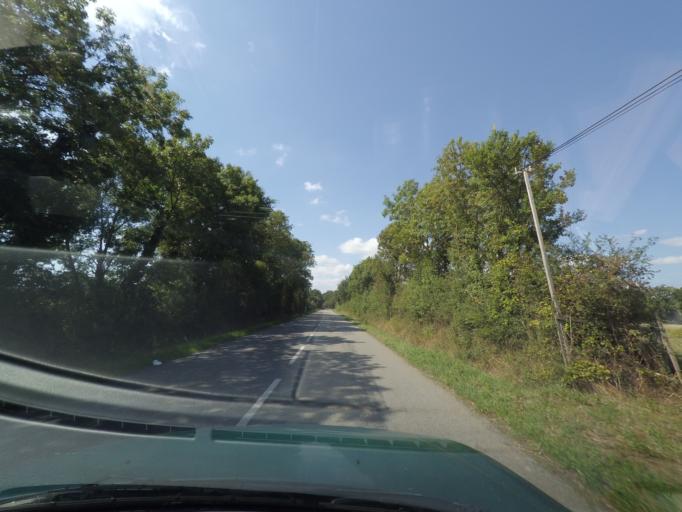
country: FR
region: Pays de la Loire
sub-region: Departement de la Loire-Atlantique
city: Sainte-Pazanne
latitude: 47.0702
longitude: -1.7748
